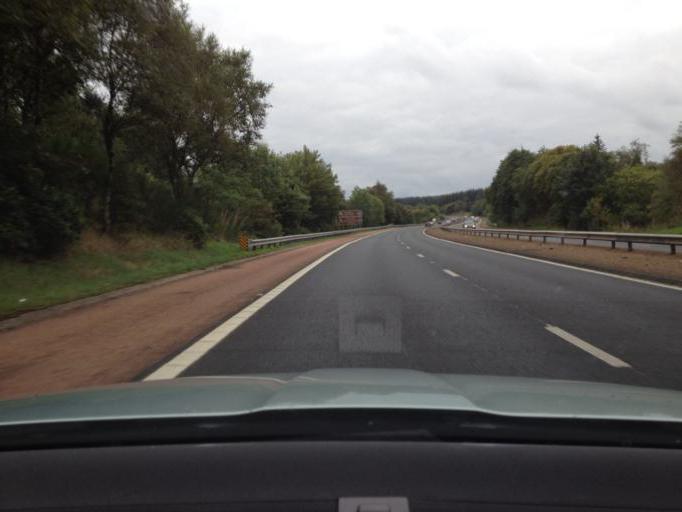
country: GB
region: Scotland
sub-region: Fife
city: Kelty
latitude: 56.1450
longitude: -3.3932
